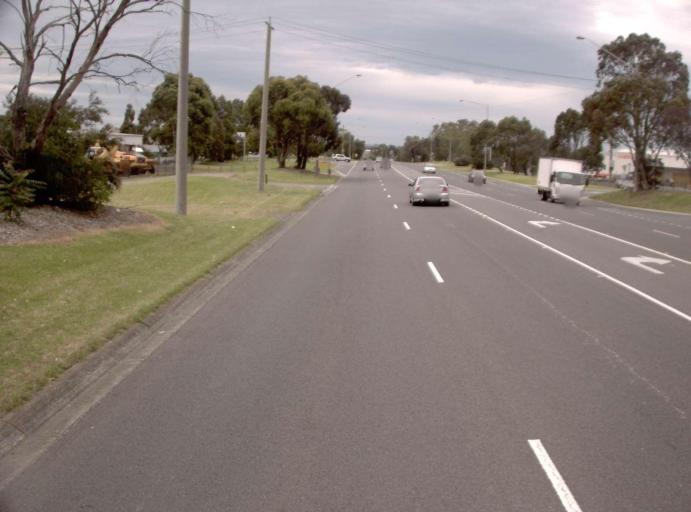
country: AU
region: Victoria
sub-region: Casey
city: Doveton
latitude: -38.0110
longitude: 145.2304
